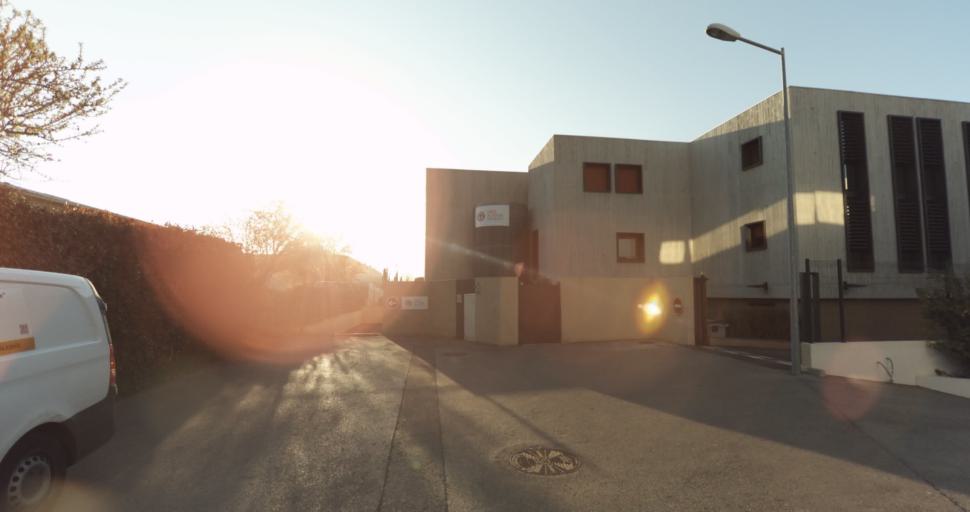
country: FR
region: Provence-Alpes-Cote d'Azur
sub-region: Departement des Bouches-du-Rhone
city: Eguilles
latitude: 43.5452
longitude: 5.3661
